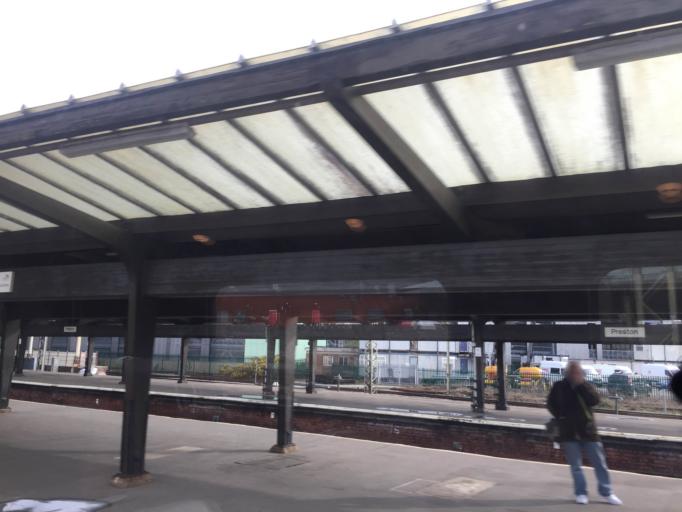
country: GB
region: England
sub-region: Lancashire
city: Preston
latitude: 53.7537
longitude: -2.7068
